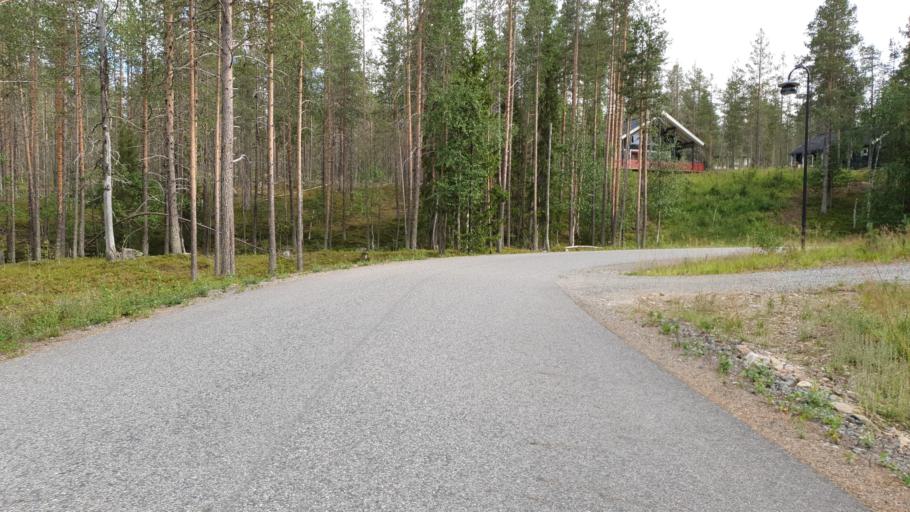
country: FI
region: Lapland
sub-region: Tunturi-Lappi
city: Kolari
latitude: 67.5926
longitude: 24.1298
